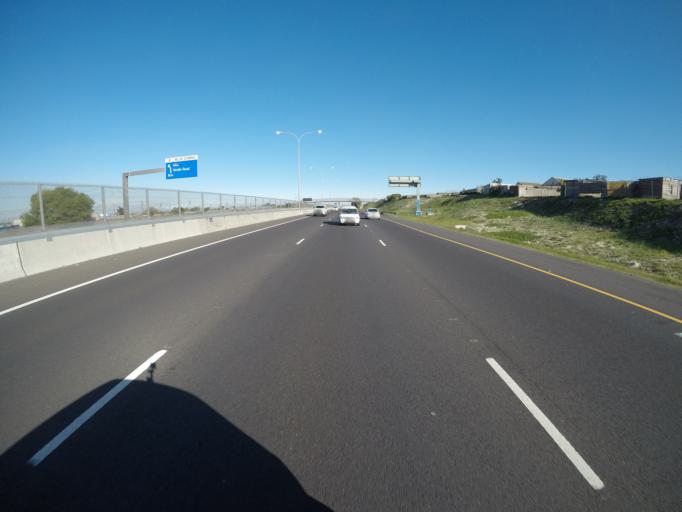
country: ZA
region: Western Cape
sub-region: City of Cape Town
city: Kraaifontein
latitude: -33.9654
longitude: 18.6551
